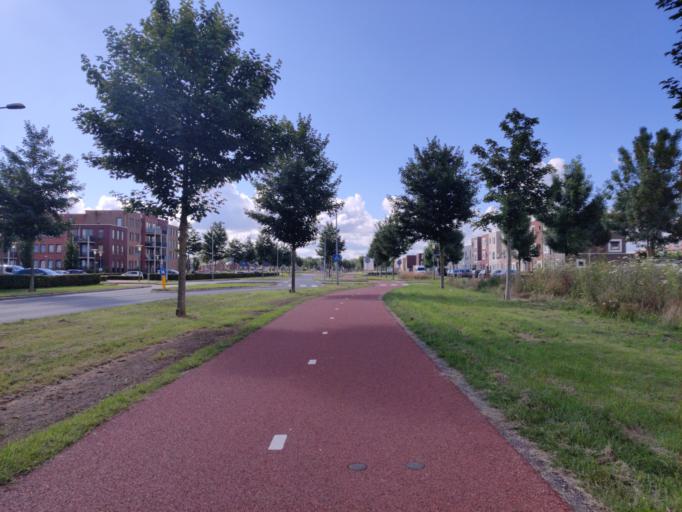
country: NL
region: Flevoland
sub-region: Gemeente Zeewolde
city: Zeewolde
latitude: 52.3449
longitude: 5.5263
